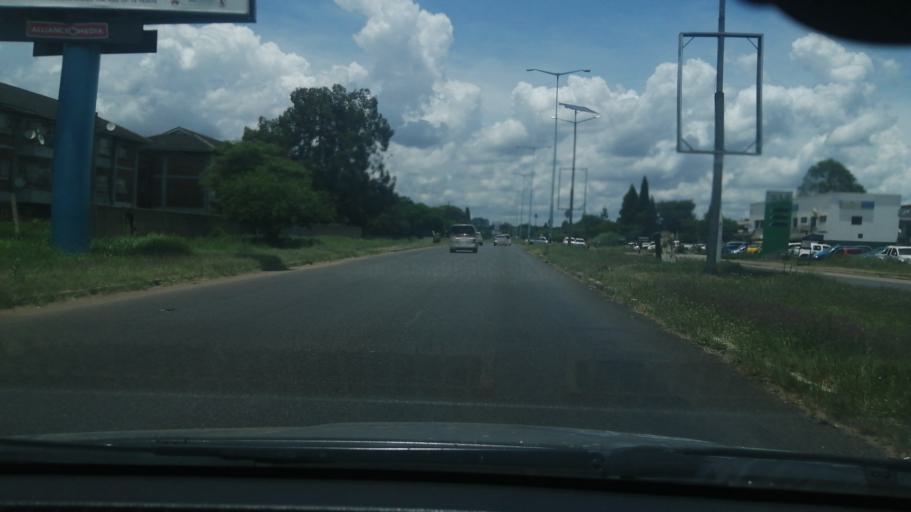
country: ZW
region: Harare
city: Harare
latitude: -17.8213
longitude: 31.0771
